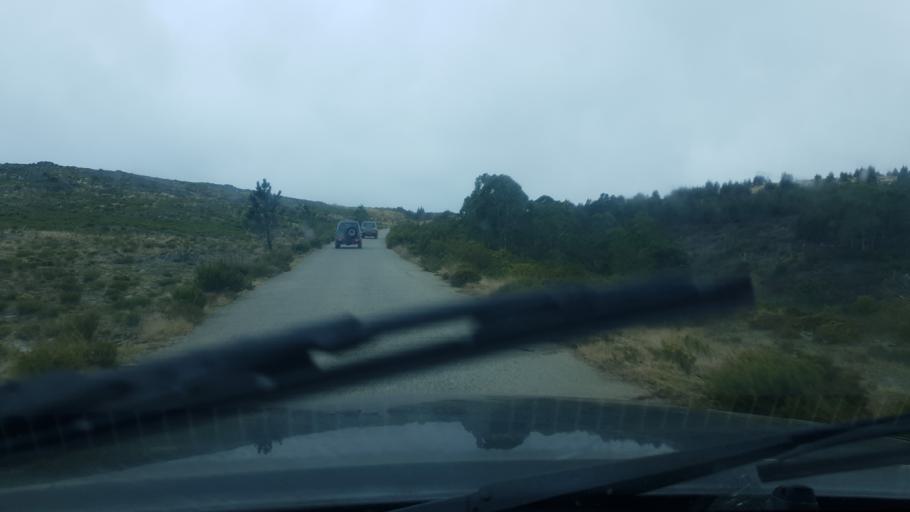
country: PT
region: Viseu
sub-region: Sao Pedro do Sul
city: Sao Pedro do Sul
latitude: 40.8545
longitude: -8.1009
